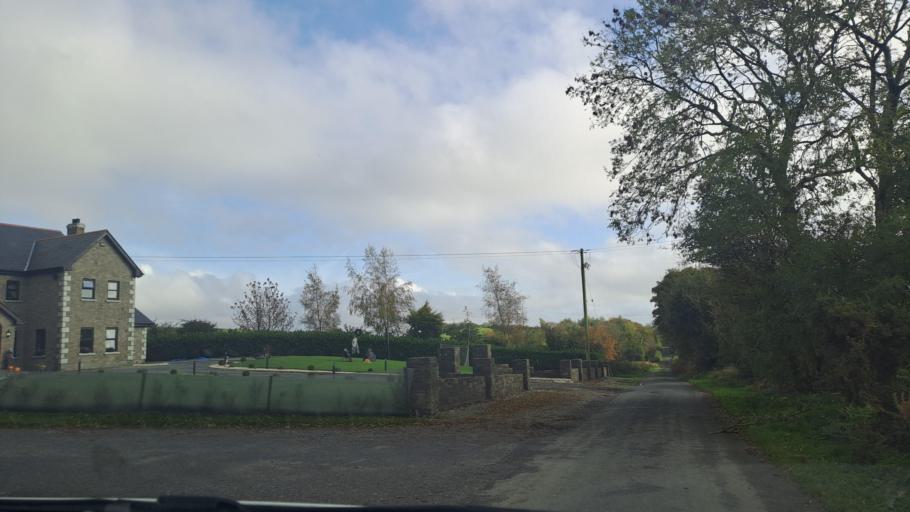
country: IE
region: Ulster
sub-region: County Monaghan
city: Carrickmacross
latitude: 54.0221
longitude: -6.7669
